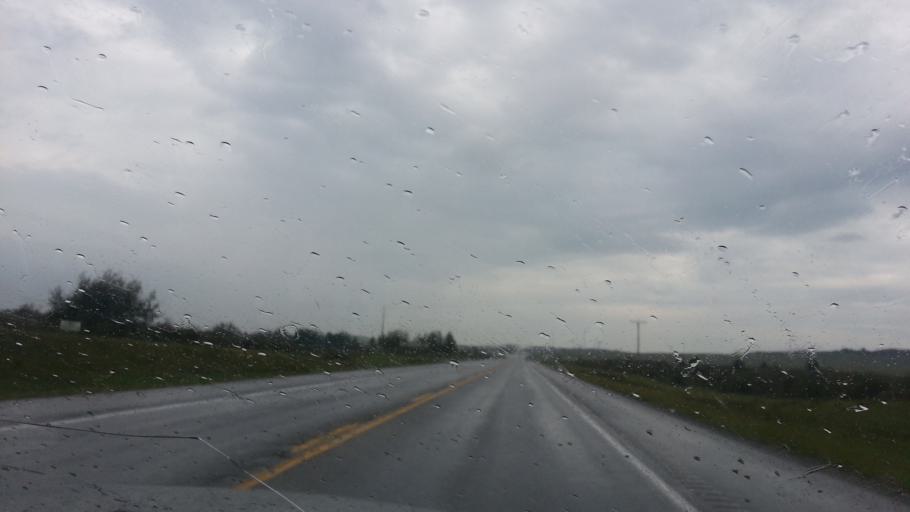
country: CA
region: Alberta
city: Cochrane
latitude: 51.0729
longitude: -114.4668
